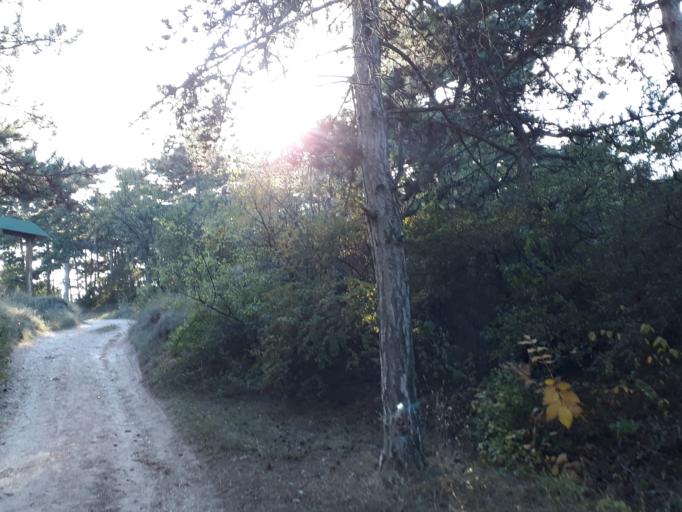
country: HU
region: Pest
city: Budaors
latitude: 47.4702
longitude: 18.9664
